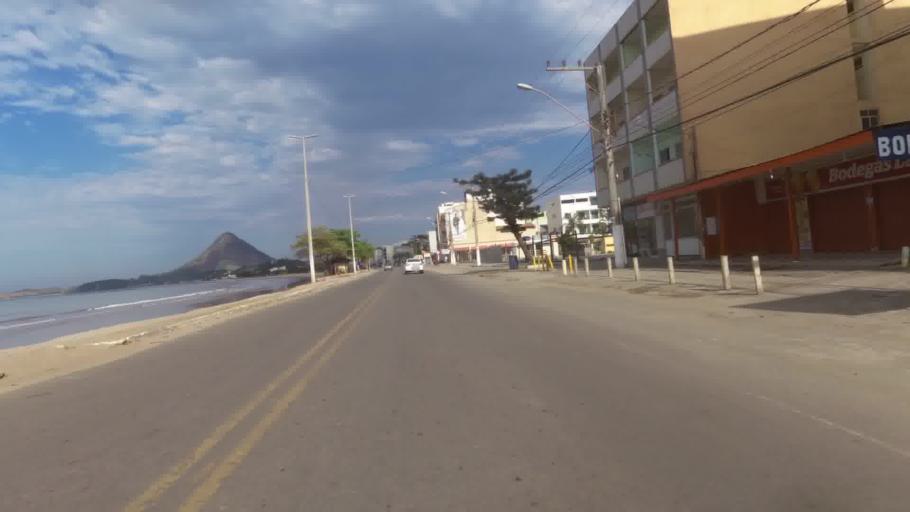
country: BR
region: Espirito Santo
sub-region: Piuma
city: Piuma
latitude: -20.8451
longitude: -40.7387
